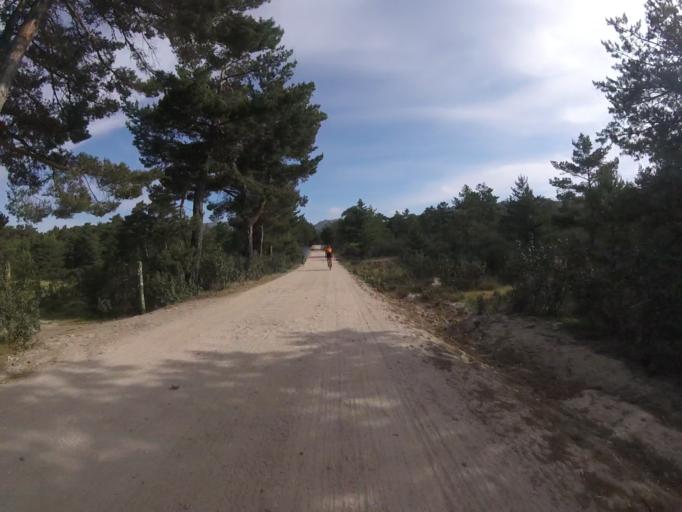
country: ES
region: Castille and Leon
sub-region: Provincia de Avila
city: Peguerinos
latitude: 40.6458
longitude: -4.1783
